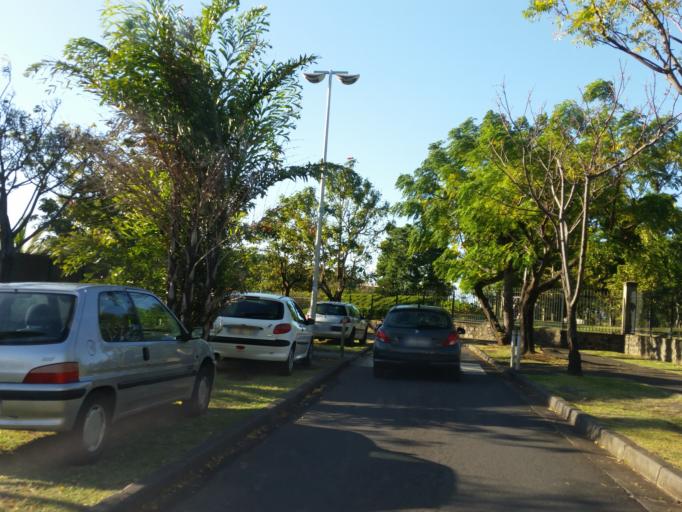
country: RE
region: Reunion
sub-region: Reunion
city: Saint-Denis
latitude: -20.8971
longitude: 55.4704
